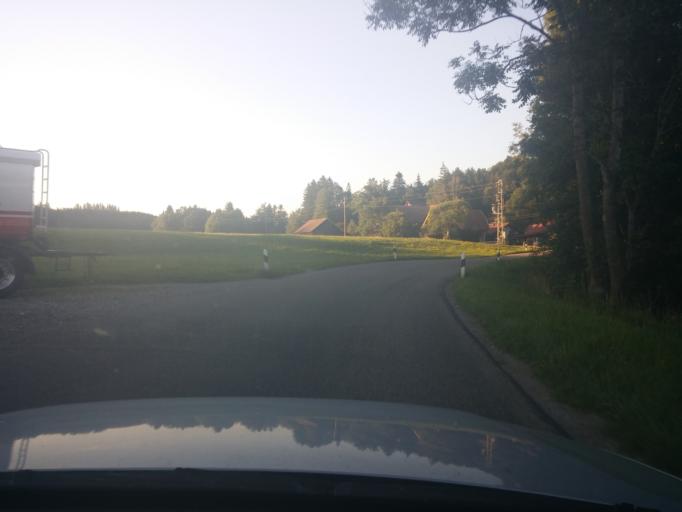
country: DE
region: Bavaria
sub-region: Swabia
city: Altusried
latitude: 47.8164
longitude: 10.1790
